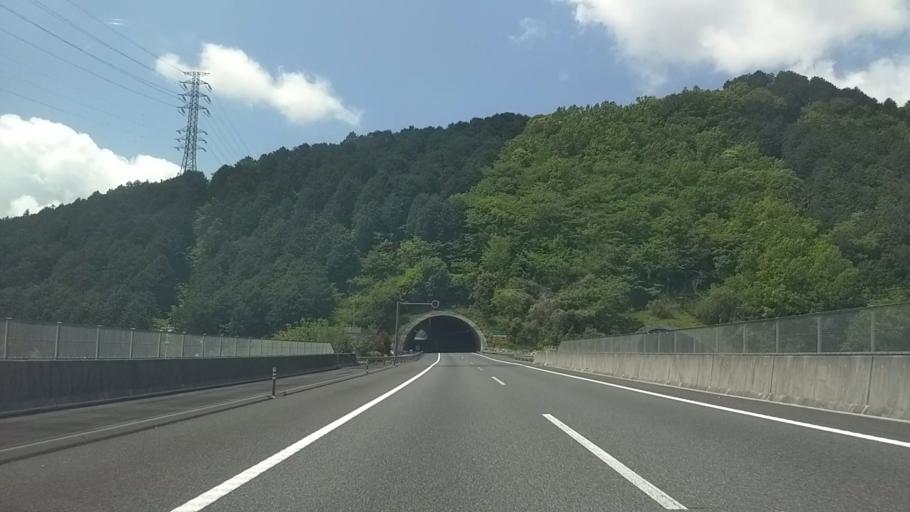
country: JP
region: Shizuoka
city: Fujinomiya
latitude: 35.1864
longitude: 138.6181
